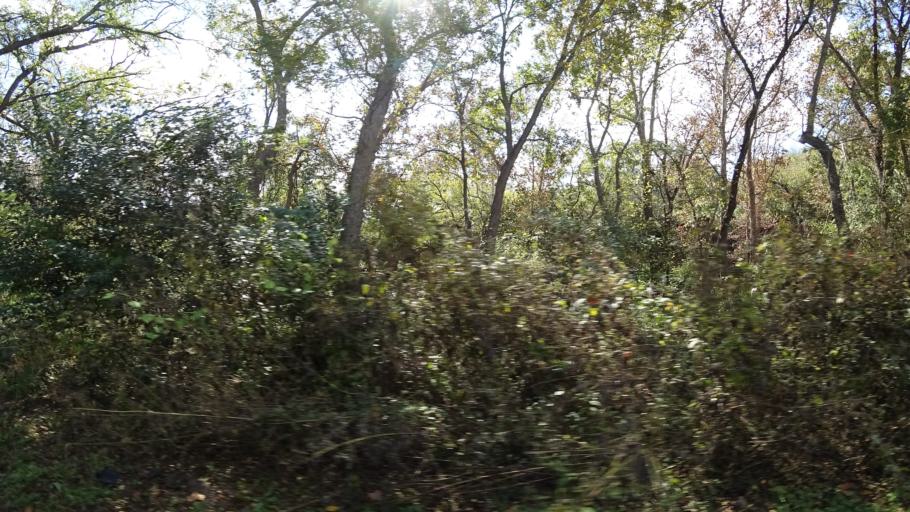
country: US
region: Texas
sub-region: Williamson County
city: Jollyville
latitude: 30.3974
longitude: -97.7796
